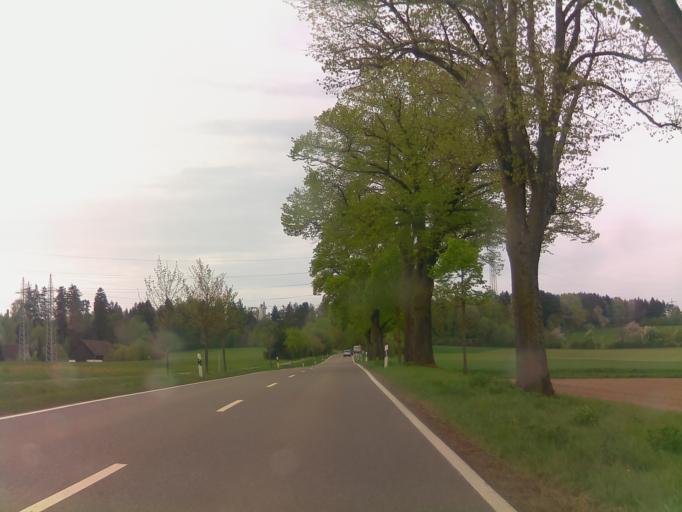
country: DE
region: Baden-Wuerttemberg
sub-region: Freiburg Region
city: Monchweiler
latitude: 48.0978
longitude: 8.4602
